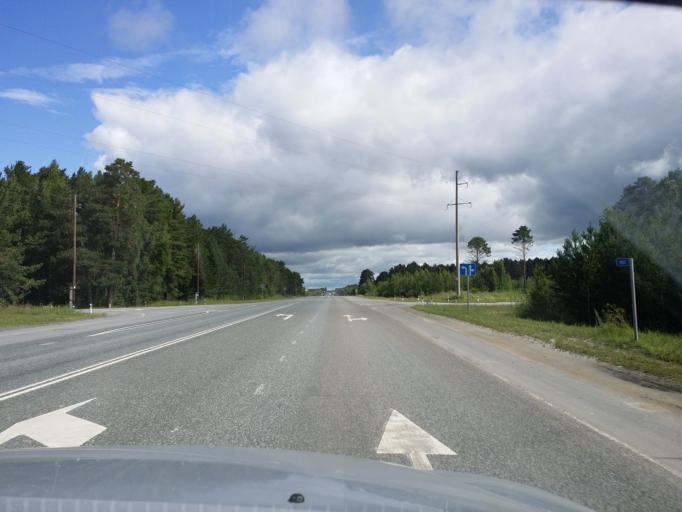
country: RU
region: Tjumen
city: Yarkovo
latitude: 57.3879
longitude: 67.0371
